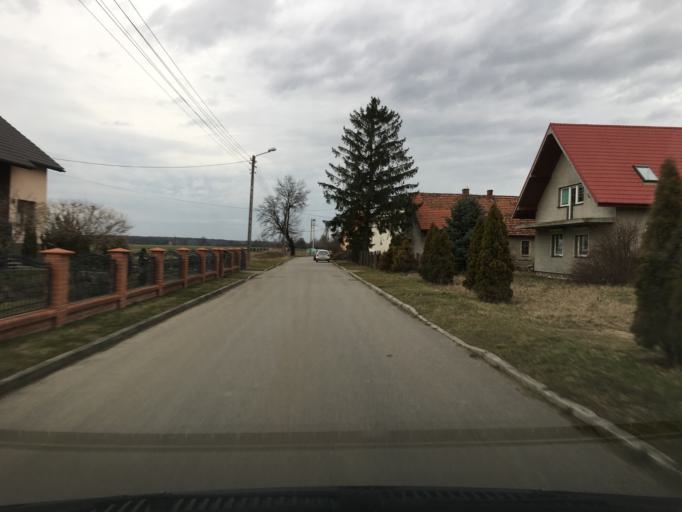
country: PL
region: Opole Voivodeship
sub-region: Powiat kedzierzynsko-kozielski
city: Wiekszyce
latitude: 50.3575
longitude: 18.1183
